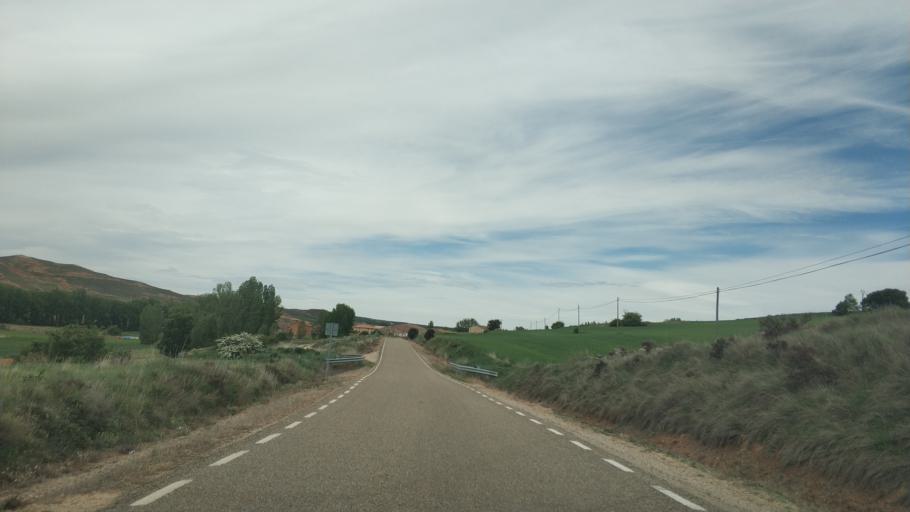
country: ES
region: Castille and Leon
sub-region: Provincia de Soria
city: Berlanga de Duero
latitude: 41.4423
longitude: -2.8259
